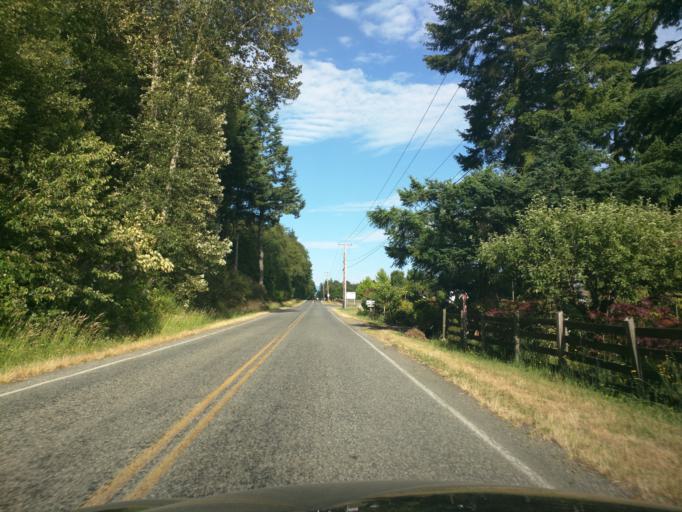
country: US
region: Washington
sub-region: Whatcom County
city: Blaine
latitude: 48.9936
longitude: -122.6596
